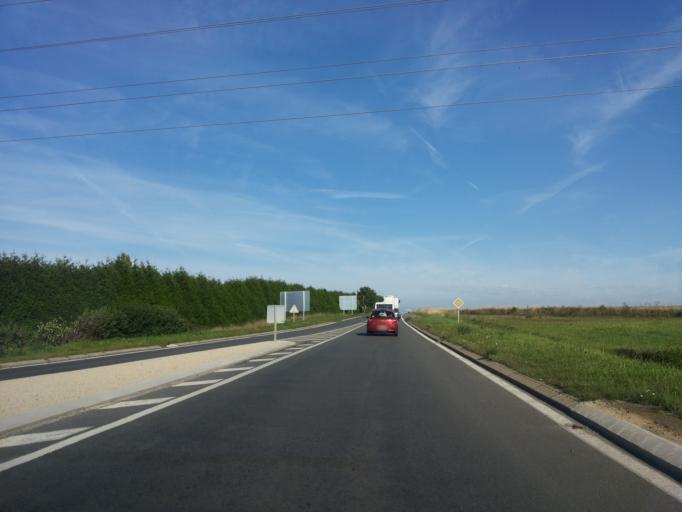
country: FR
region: Picardie
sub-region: Departement de l'Aisne
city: Charmes
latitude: 49.6455
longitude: 3.3952
